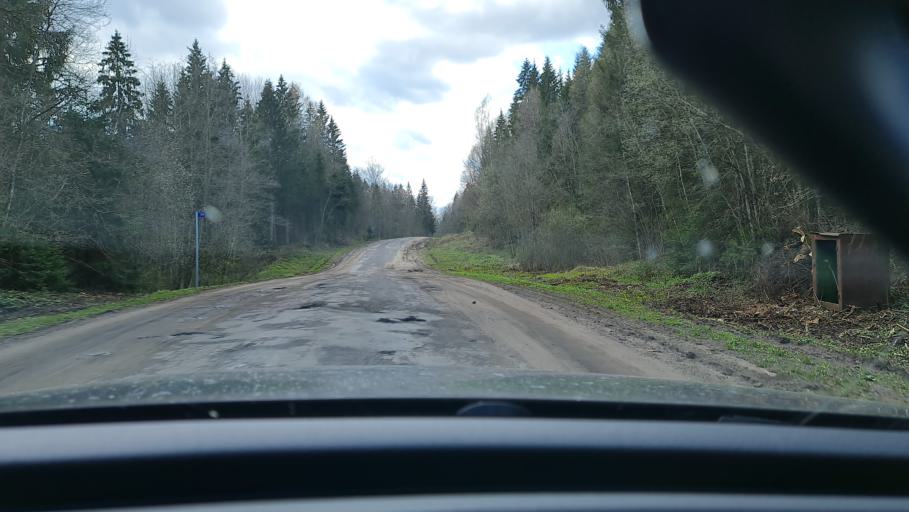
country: RU
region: Tverskaya
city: Toropets
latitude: 56.6251
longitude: 31.4317
